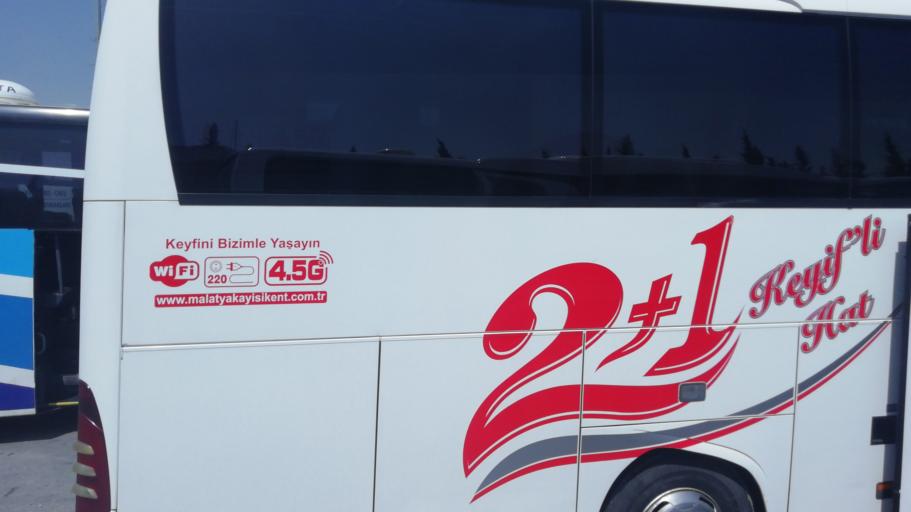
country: TR
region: Kocaeli
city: Gebze
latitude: 40.7953
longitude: 29.4595
